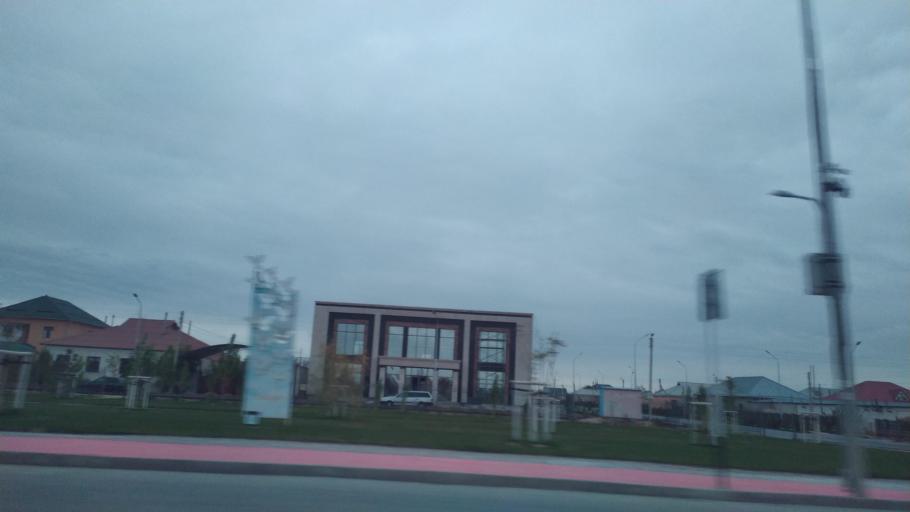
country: KZ
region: Ongtustik Qazaqstan
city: Turkestan
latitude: 43.2819
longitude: 68.3167
